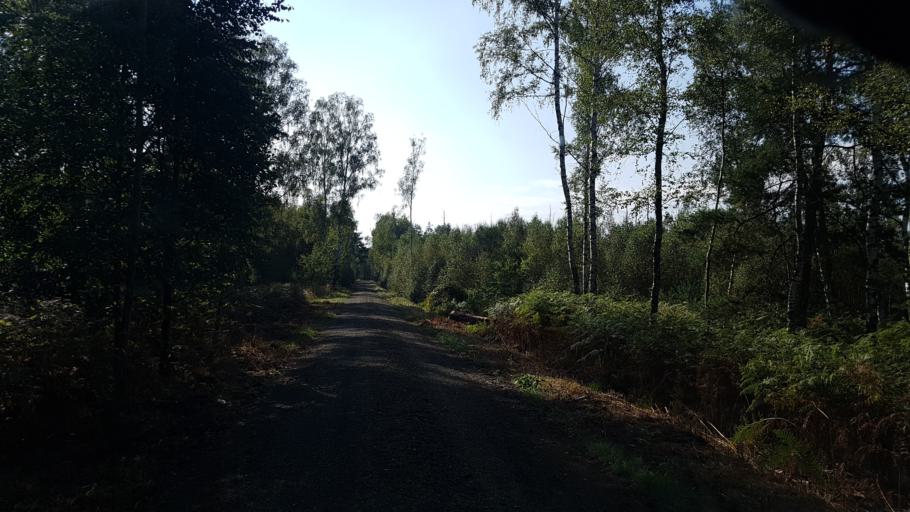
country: DE
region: Brandenburg
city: Plessa
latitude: 51.5162
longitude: 13.6400
